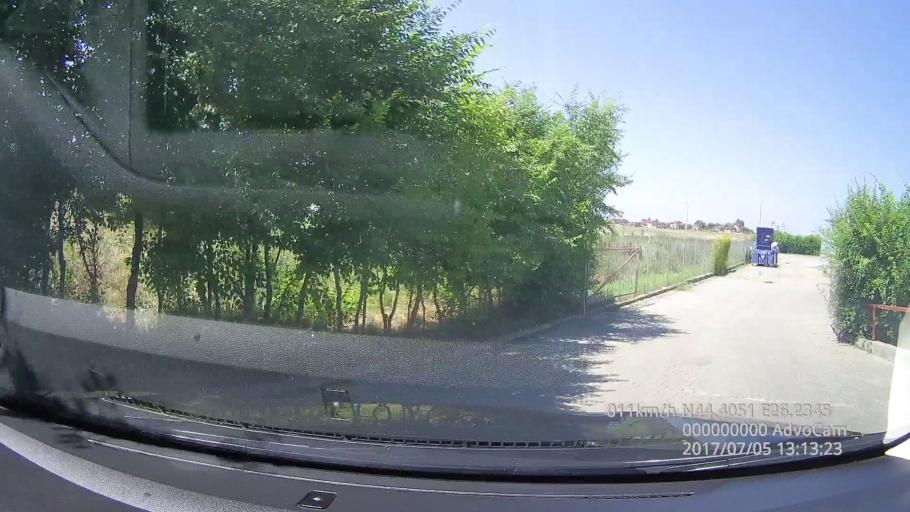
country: RO
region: Ilfov
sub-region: Comuna Glina
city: Catelu
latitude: 44.4050
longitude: 26.2345
